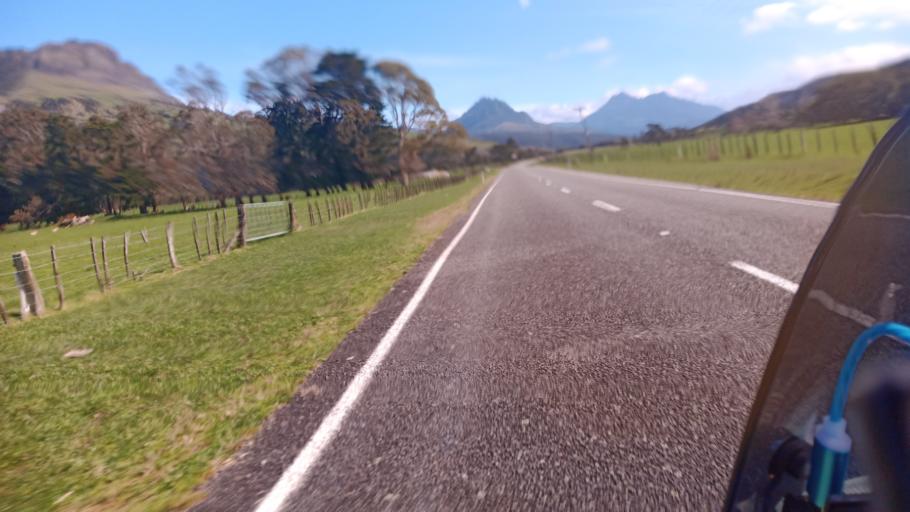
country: NZ
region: Gisborne
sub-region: Gisborne District
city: Gisborne
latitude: -37.8655
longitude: 178.2150
